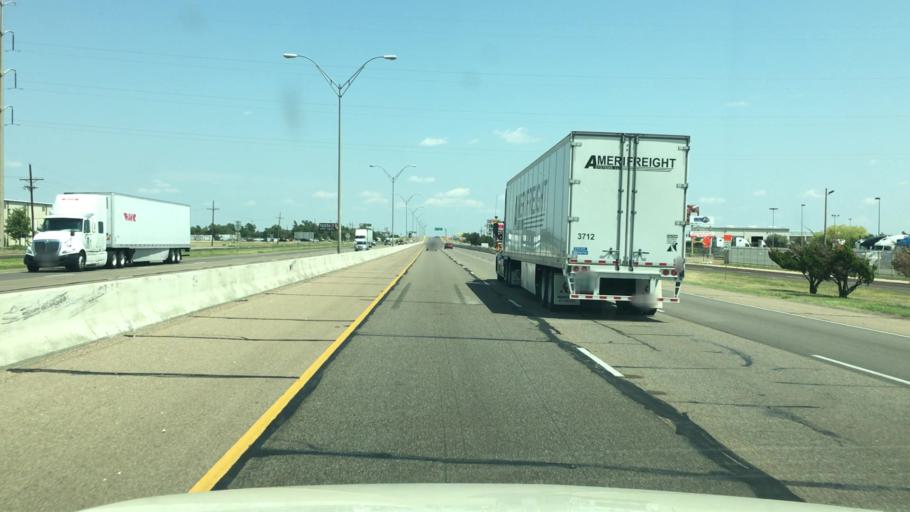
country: US
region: Texas
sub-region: Potter County
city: Amarillo
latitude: 35.1926
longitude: -101.7702
